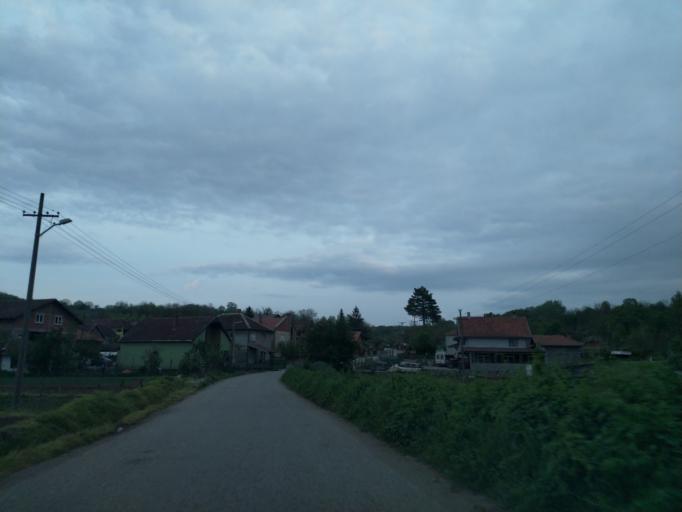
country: RS
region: Central Serbia
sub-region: Pomoravski Okrug
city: Cuprija
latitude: 43.9588
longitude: 21.4740
